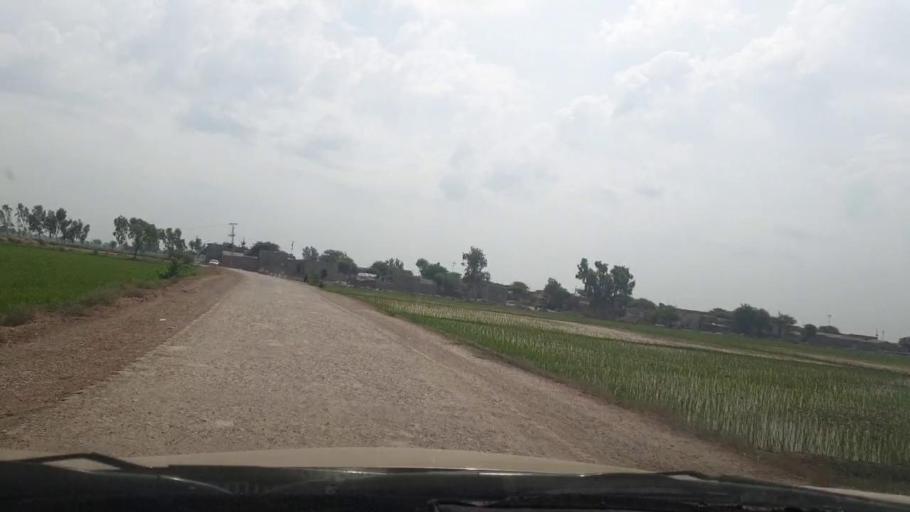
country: PK
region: Sindh
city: Larkana
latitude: 27.6775
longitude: 68.1904
